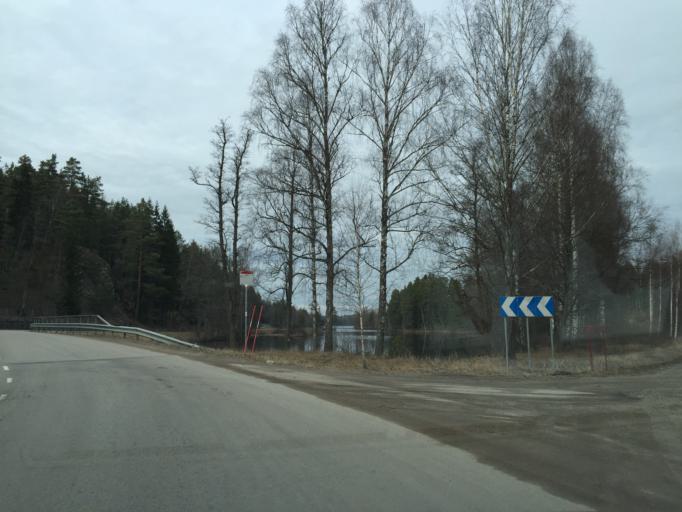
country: SE
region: OEstergoetland
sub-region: Finspangs Kommun
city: Finspang
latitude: 58.7492
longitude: 15.8285
